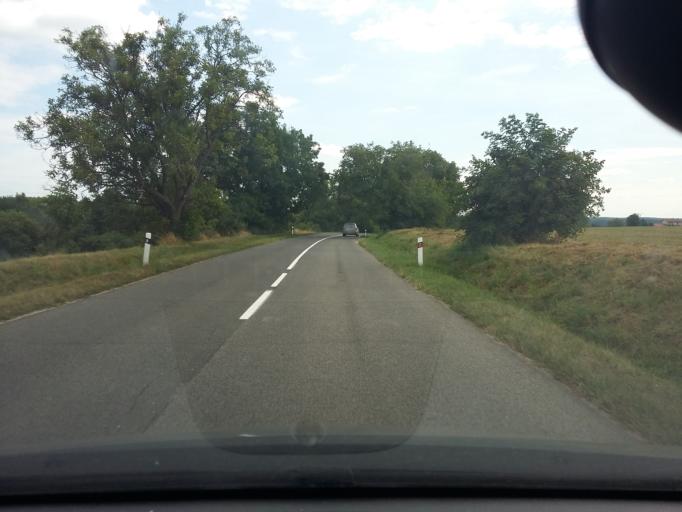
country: SK
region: Trnavsky
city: Gbely
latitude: 48.6556
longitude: 17.1441
